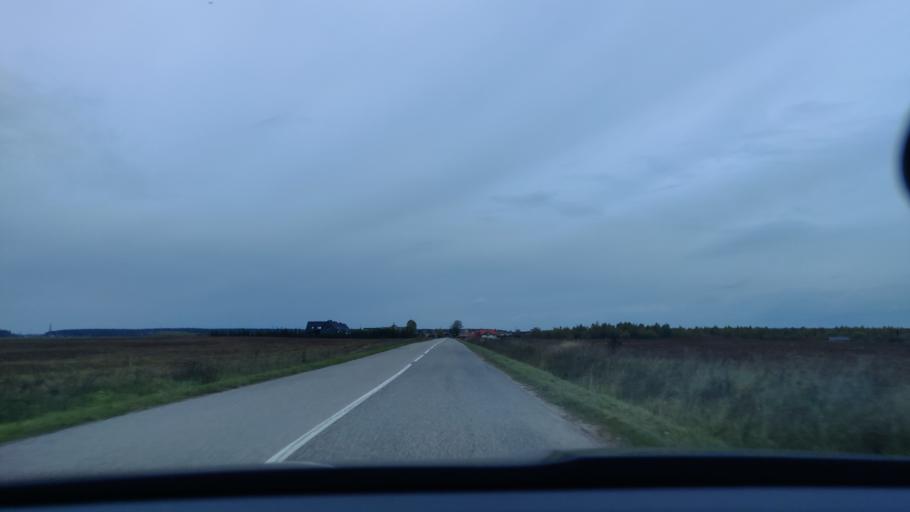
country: LT
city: Lentvaris
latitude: 54.5760
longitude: 25.0520
